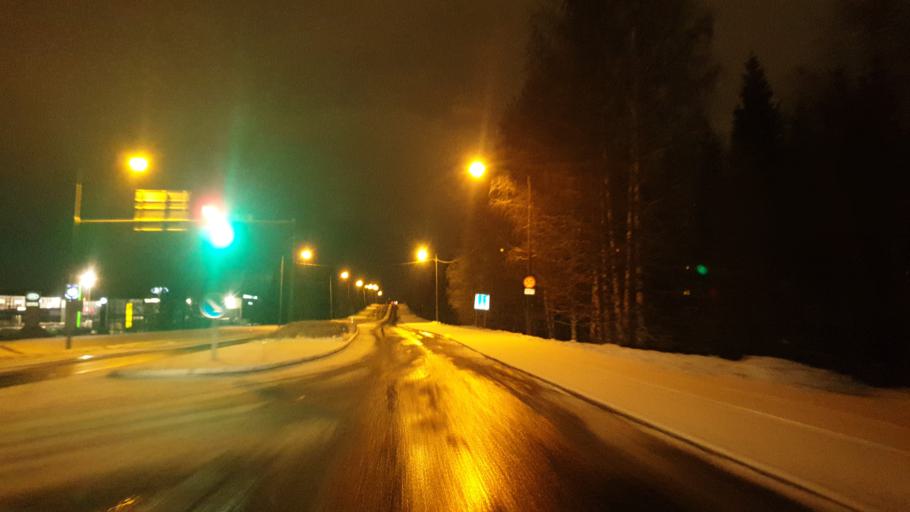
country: FI
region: Northern Ostrobothnia
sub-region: Oulu
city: Oulu
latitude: 64.9858
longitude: 25.4753
